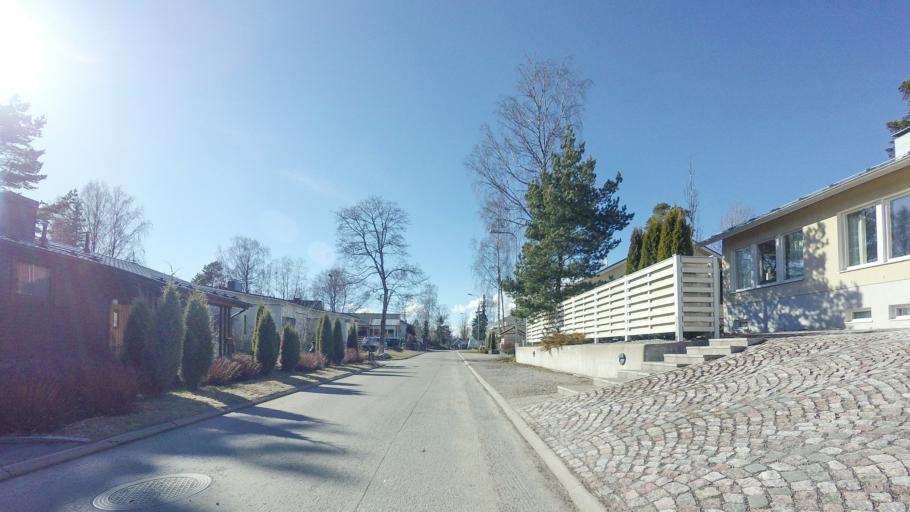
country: FI
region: Uusimaa
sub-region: Helsinki
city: Helsinki
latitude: 60.1626
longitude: 25.0653
